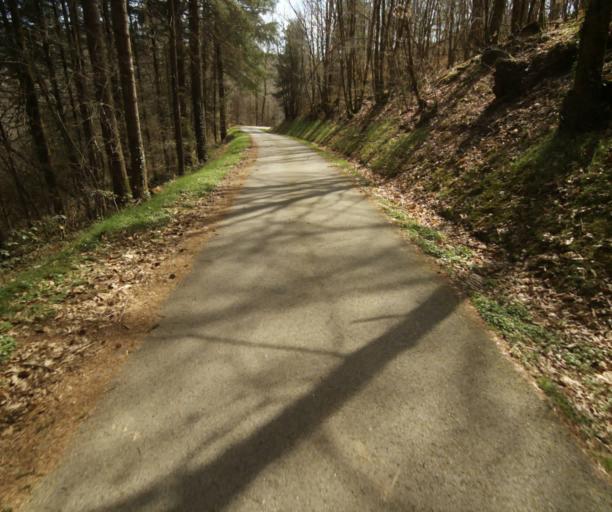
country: FR
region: Limousin
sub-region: Departement de la Correze
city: Naves
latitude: 45.3451
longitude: 1.8033
